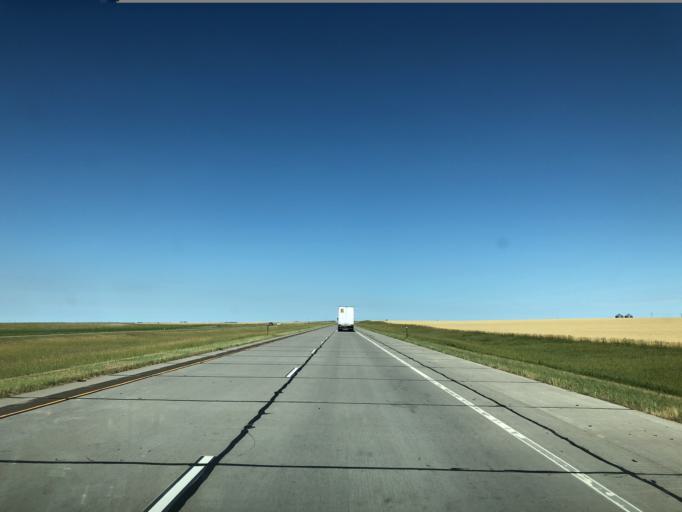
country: US
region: Colorado
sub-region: Kit Carson County
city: Burlington
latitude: 39.2949
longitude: -102.4888
